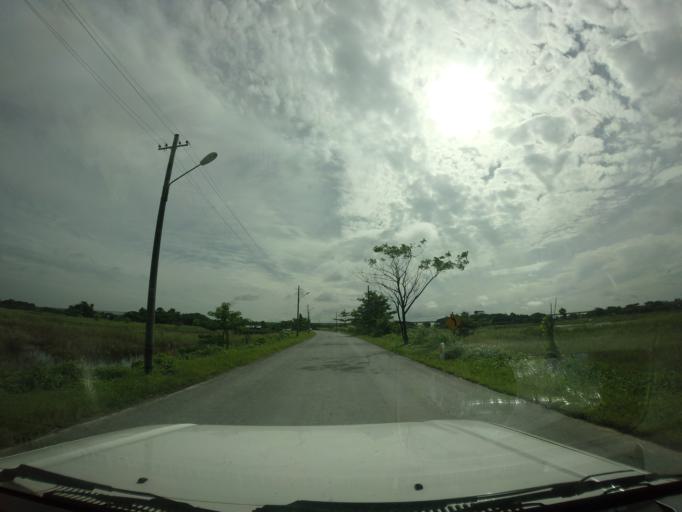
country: MM
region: Ayeyarwady
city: Nyaungdon
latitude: 17.0173
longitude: 95.5785
